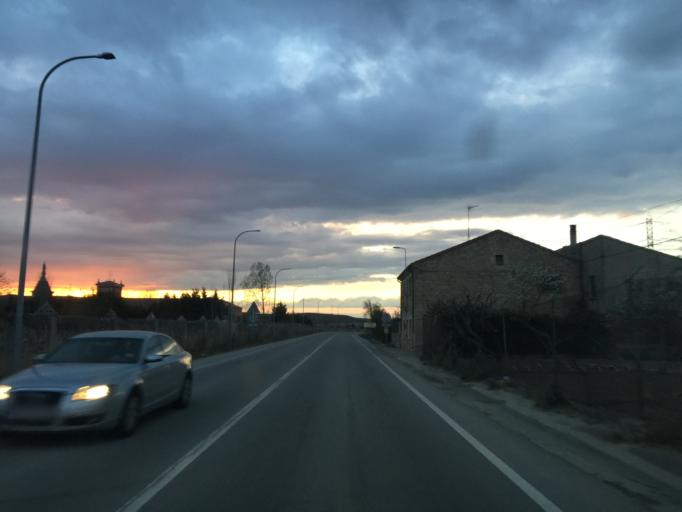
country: ES
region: Castille and Leon
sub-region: Provincia de Burgos
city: Tardajos
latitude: 42.3501
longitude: -3.8162
